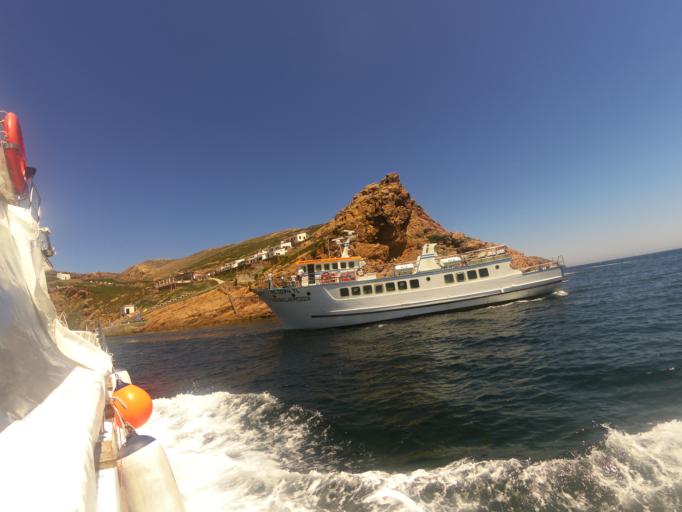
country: PT
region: Leiria
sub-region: Peniche
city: Peniche
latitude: 39.4130
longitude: -9.5058
